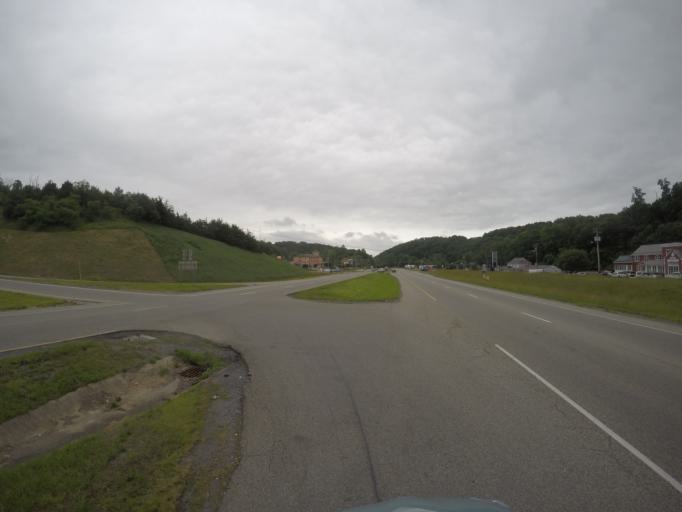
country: US
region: Virginia
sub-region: Augusta County
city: Jolivue
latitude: 38.1265
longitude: -79.0339
